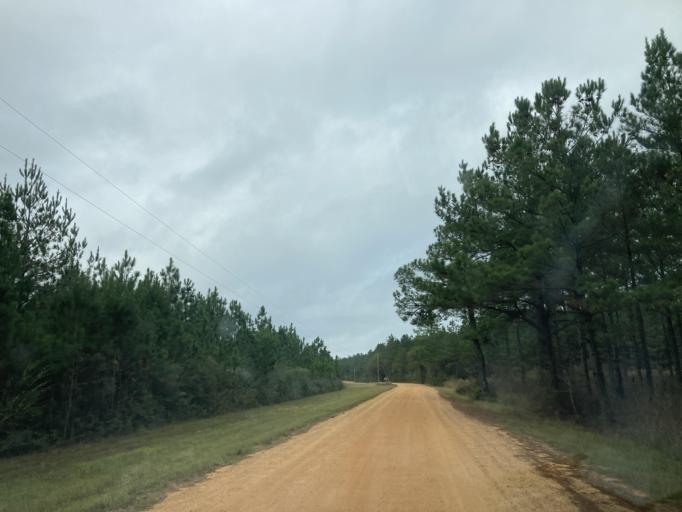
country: US
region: Mississippi
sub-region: Lamar County
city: Lumberton
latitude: 31.0238
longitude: -89.5720
